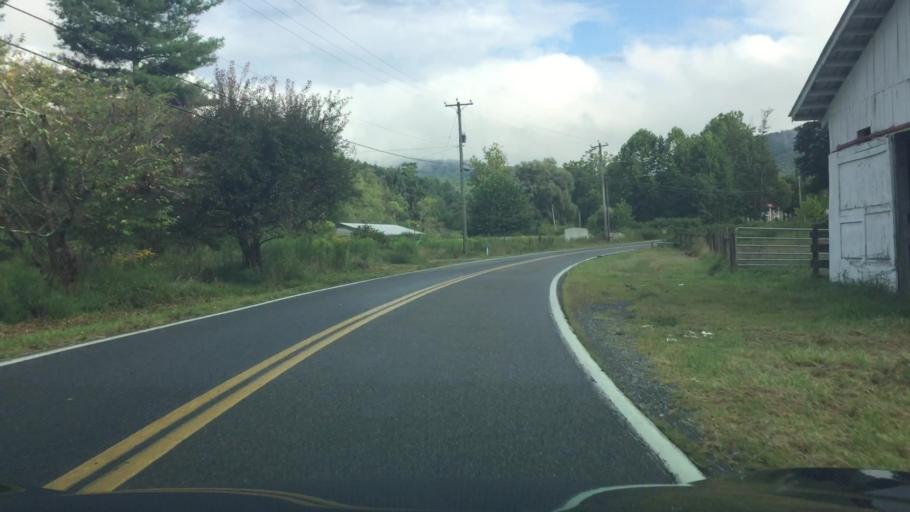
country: US
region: Virginia
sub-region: Smyth County
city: Atkins
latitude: 36.8547
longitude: -81.4284
